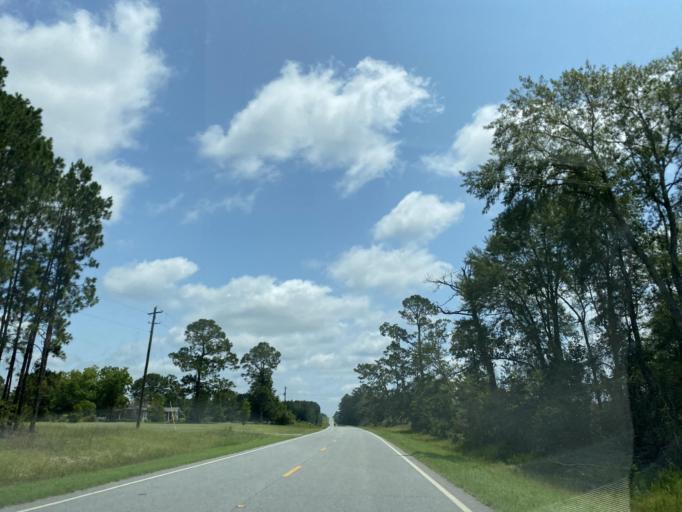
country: US
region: Georgia
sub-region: Telfair County
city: Helena
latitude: 32.0302
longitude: -83.0062
